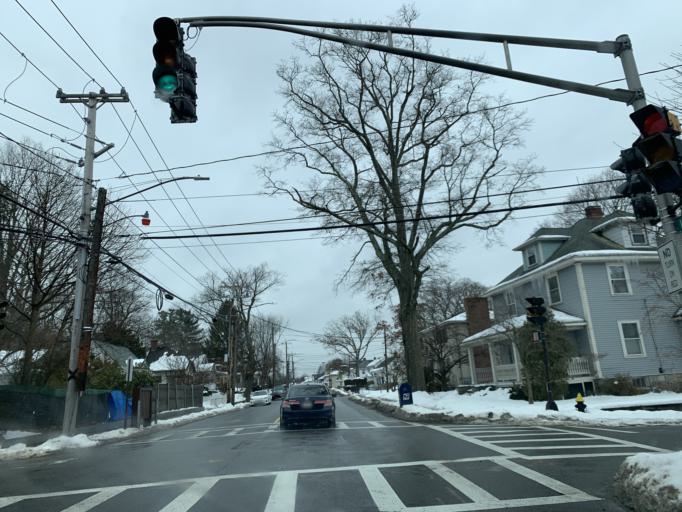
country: US
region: Massachusetts
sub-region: Norfolk County
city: Dedham
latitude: 42.2876
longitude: -71.1655
